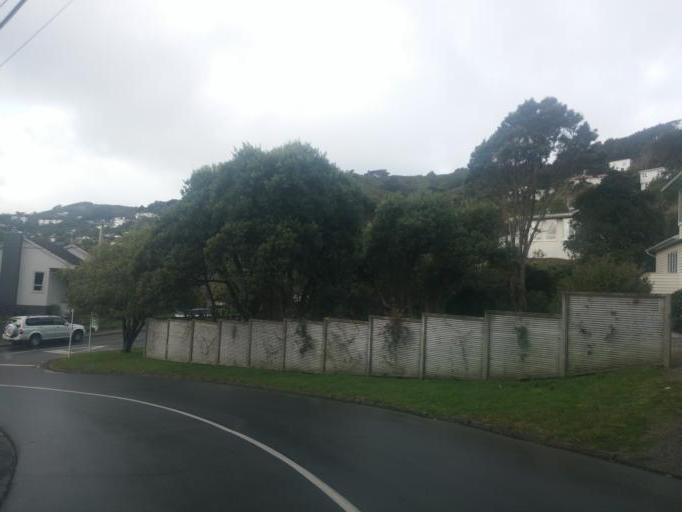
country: NZ
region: Wellington
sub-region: Wellington City
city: Kelburn
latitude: -41.2700
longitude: 174.7584
